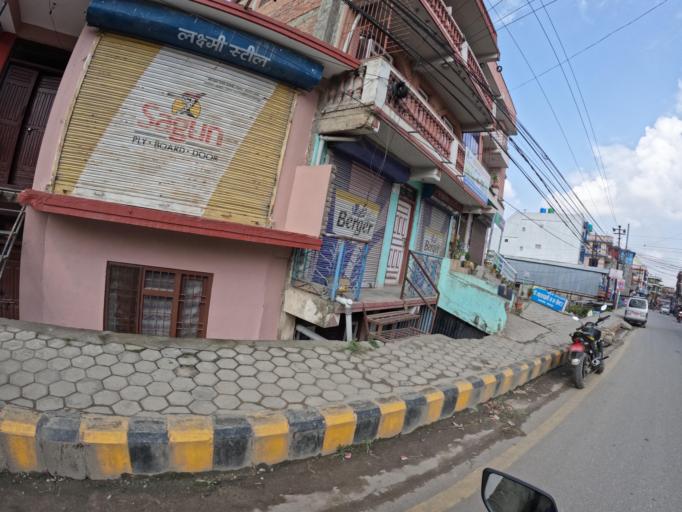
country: NP
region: Central Region
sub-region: Bagmati Zone
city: Patan
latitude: 27.6638
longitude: 85.3671
